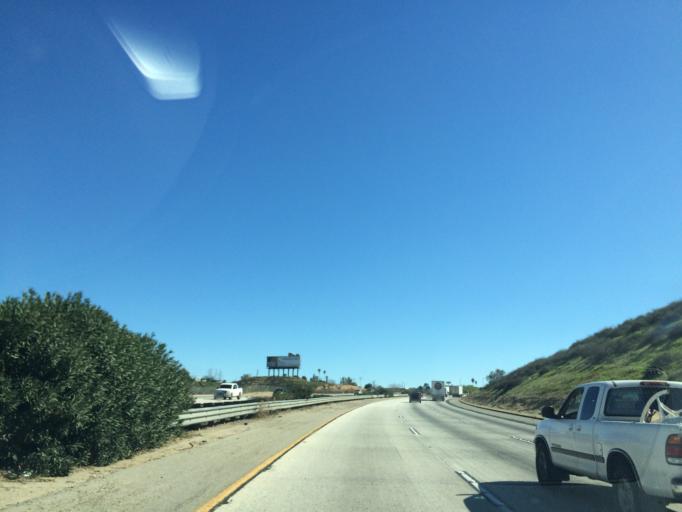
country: US
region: California
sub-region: Riverside County
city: Calimesa
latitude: 34.0113
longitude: -117.0707
